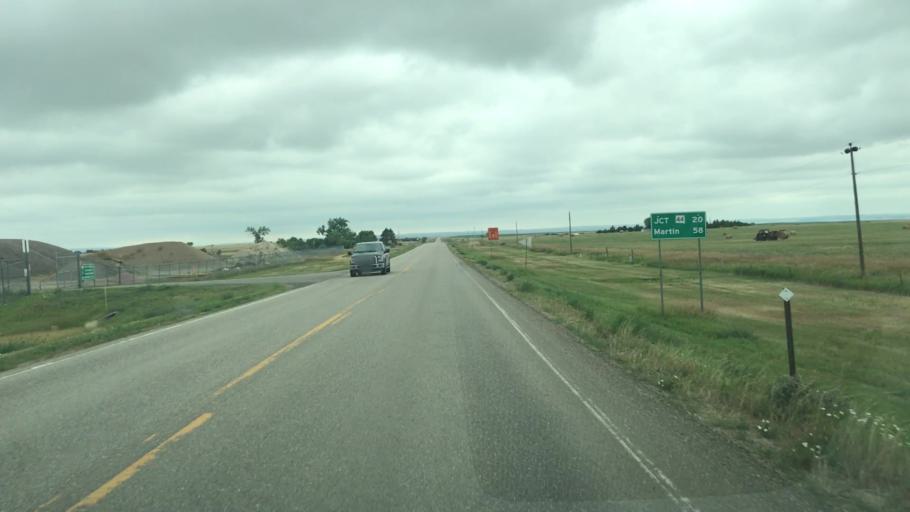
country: US
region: South Dakota
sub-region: Jackson County
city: Kadoka
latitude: 43.8333
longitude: -101.5225
